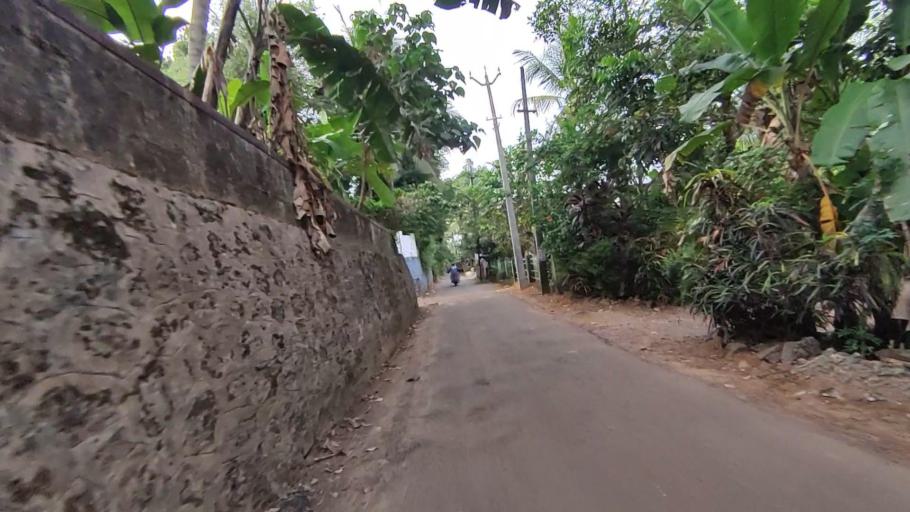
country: IN
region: Kerala
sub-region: Kottayam
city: Kottayam
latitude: 9.6088
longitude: 76.4850
